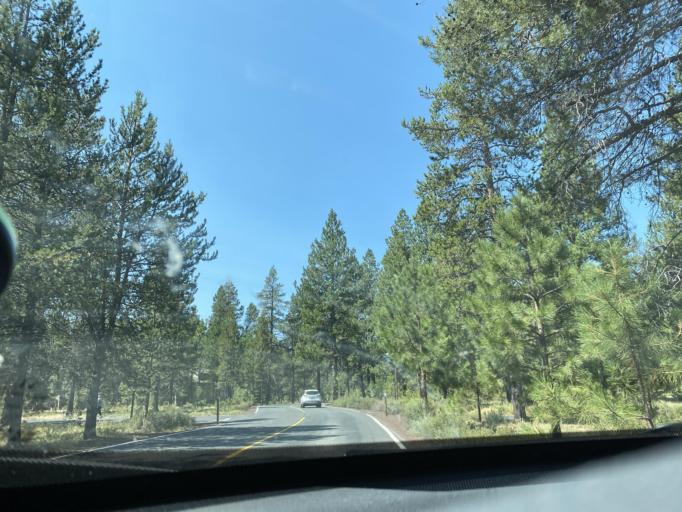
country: US
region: Oregon
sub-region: Deschutes County
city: Sunriver
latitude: 43.8909
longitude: -121.4257
